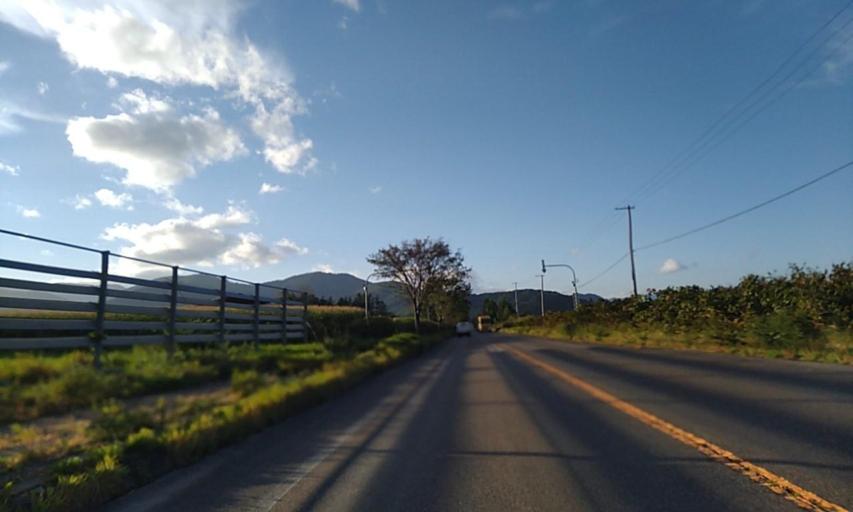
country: JP
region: Hokkaido
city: Otofuke
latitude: 42.9857
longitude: 142.8570
